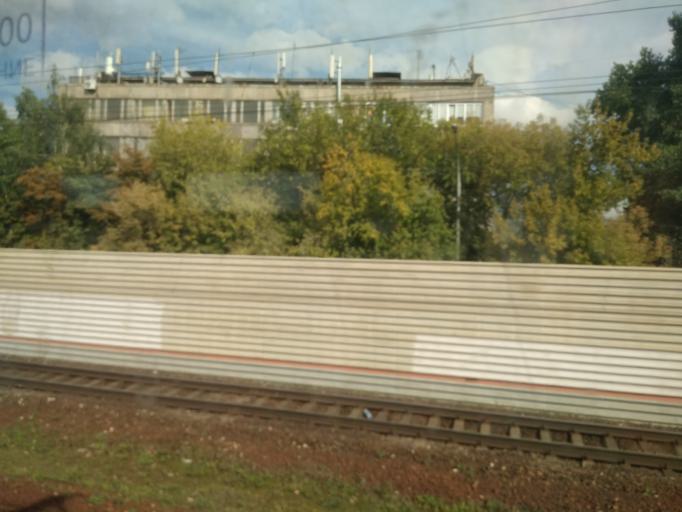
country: RU
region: Moscow
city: Lefortovo
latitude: 55.7597
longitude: 37.7193
